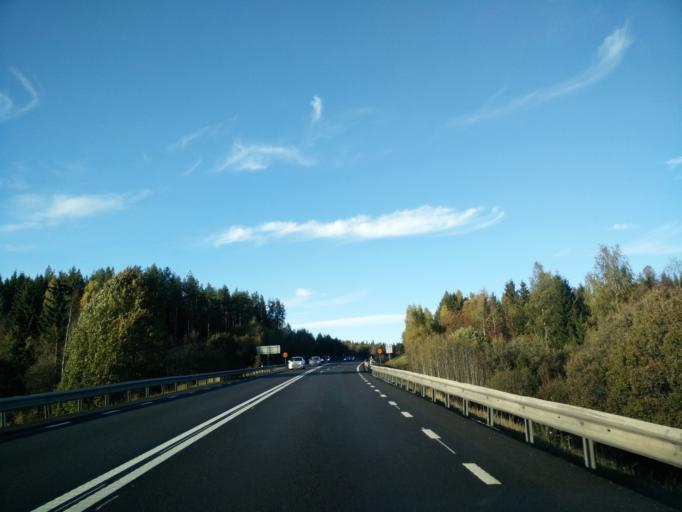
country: SE
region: Gaevleborg
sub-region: Nordanstigs Kommun
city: Bergsjoe
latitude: 62.0617
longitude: 17.2659
